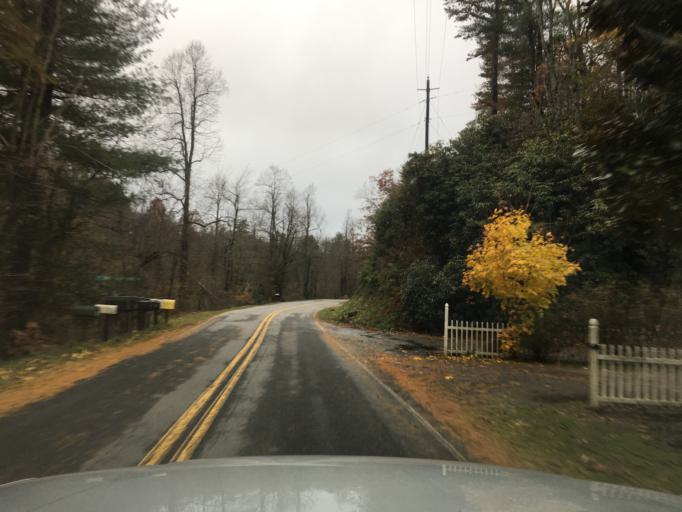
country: US
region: North Carolina
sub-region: Rutherford County
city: Lake Lure
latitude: 35.5326
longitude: -82.2371
